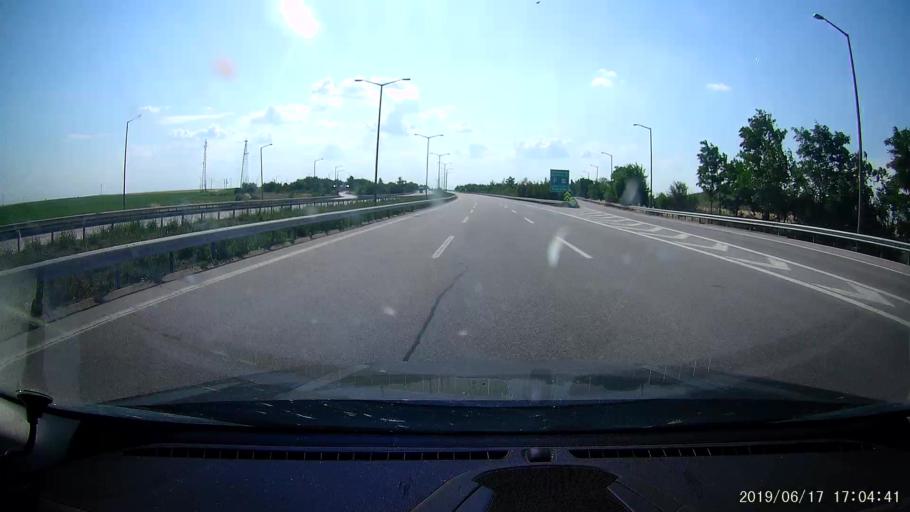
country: TR
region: Edirne
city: Haskoy
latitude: 41.6567
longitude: 26.7203
